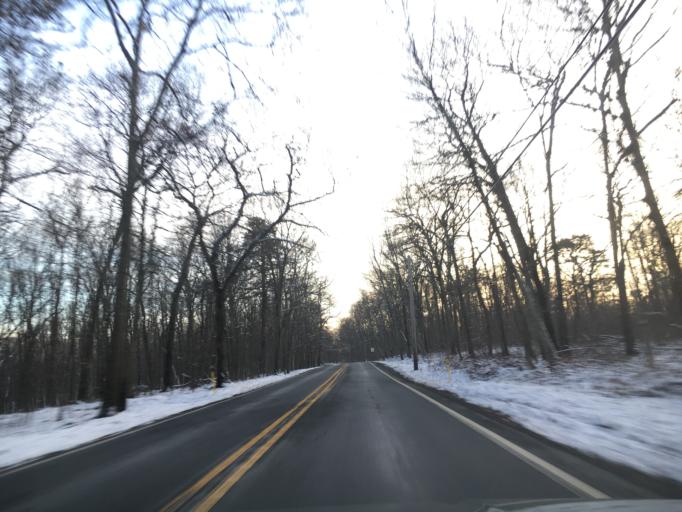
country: US
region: Pennsylvania
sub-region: Pike County
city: Saw Creek
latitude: 41.1462
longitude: -75.0815
